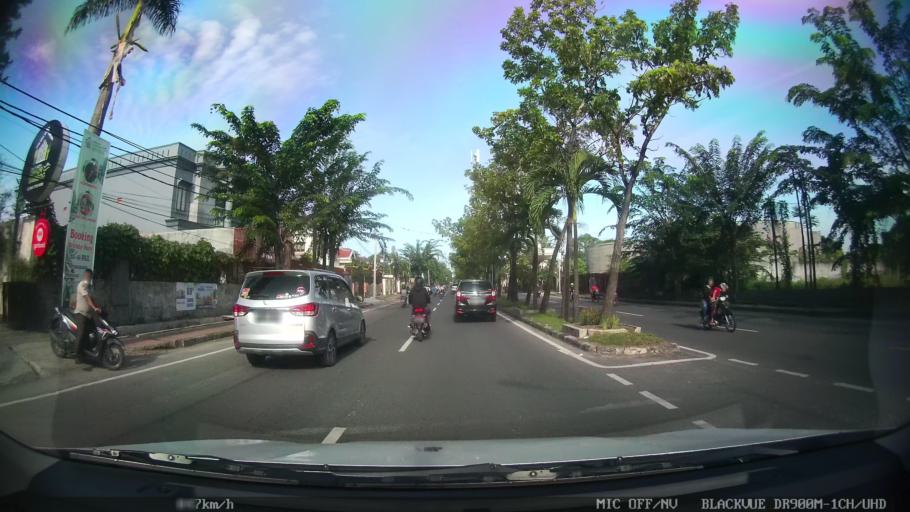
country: ID
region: North Sumatra
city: Medan
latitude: 3.6079
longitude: 98.6513
